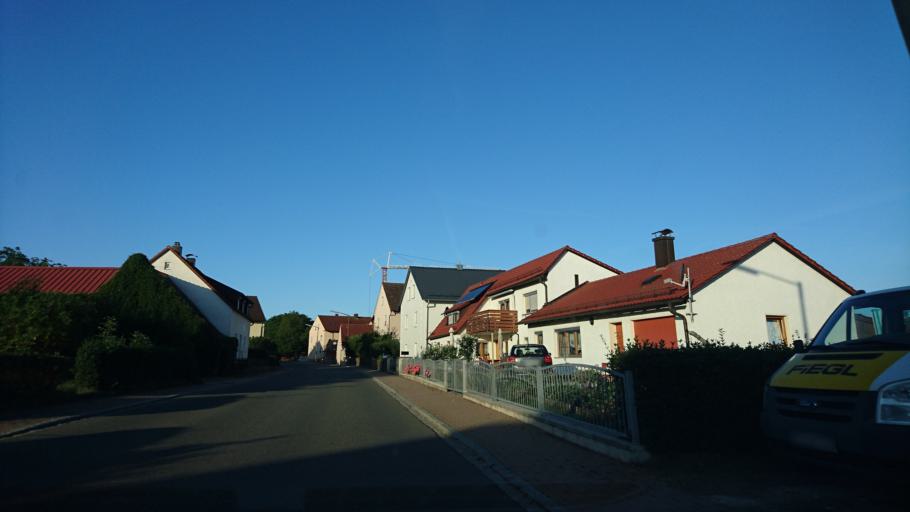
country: DE
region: Bavaria
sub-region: Regierungsbezirk Mittelfranken
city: Burgsalach
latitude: 49.0357
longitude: 11.1025
